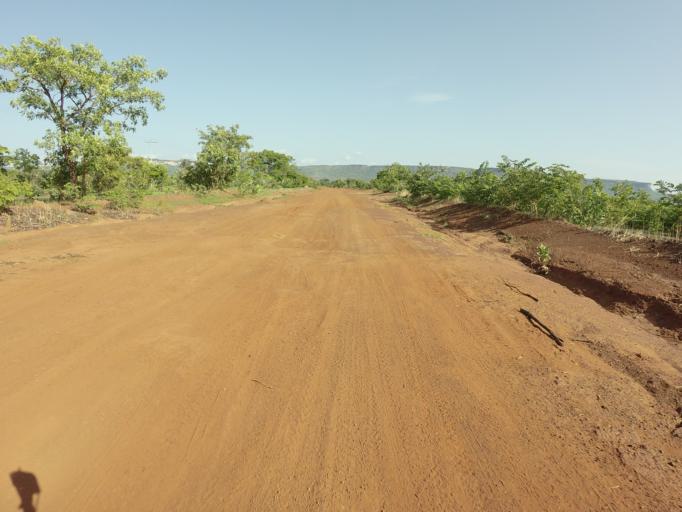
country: GH
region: Upper East
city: Bawku
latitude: 10.6852
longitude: -0.2154
